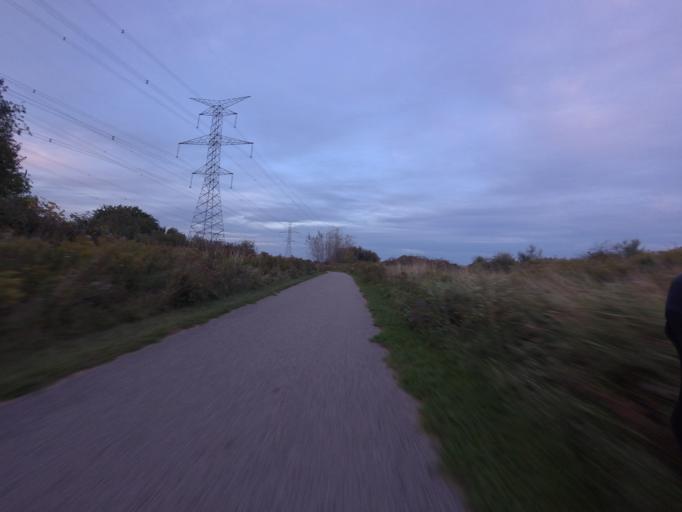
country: CA
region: Ontario
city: Oshawa
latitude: 43.8986
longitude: -78.6319
